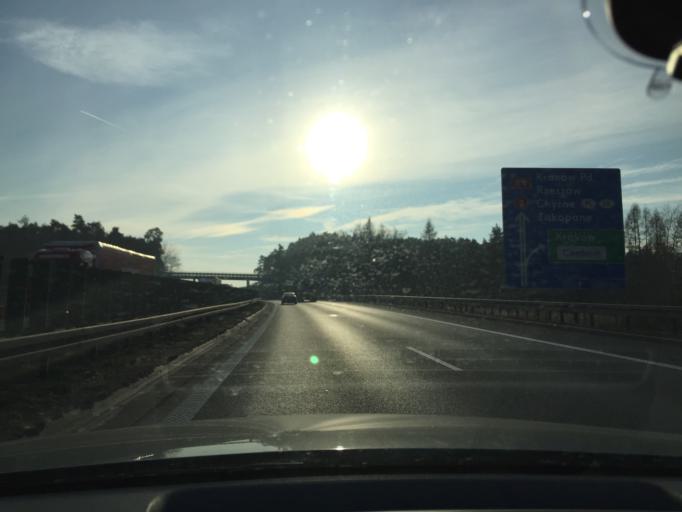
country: PL
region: Lesser Poland Voivodeship
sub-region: Powiat krakowski
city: Kryspinow
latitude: 50.0487
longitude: 19.8073
